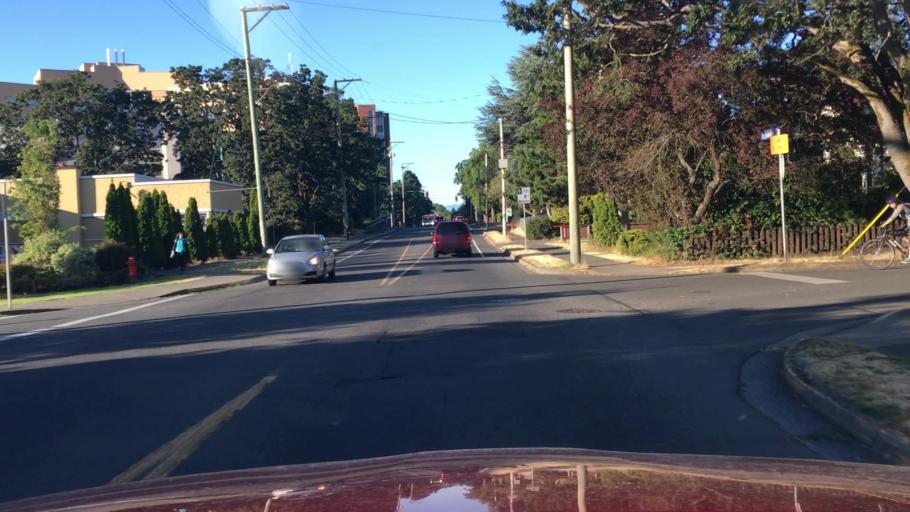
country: CA
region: British Columbia
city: Oak Bay
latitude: 48.4353
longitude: -123.3289
